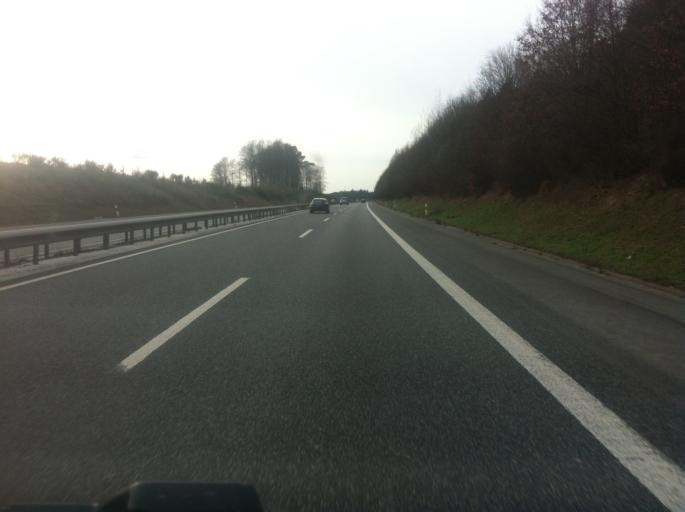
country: DE
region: Rheinland-Pfalz
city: Unzenberg
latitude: 49.9585
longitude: 7.4447
